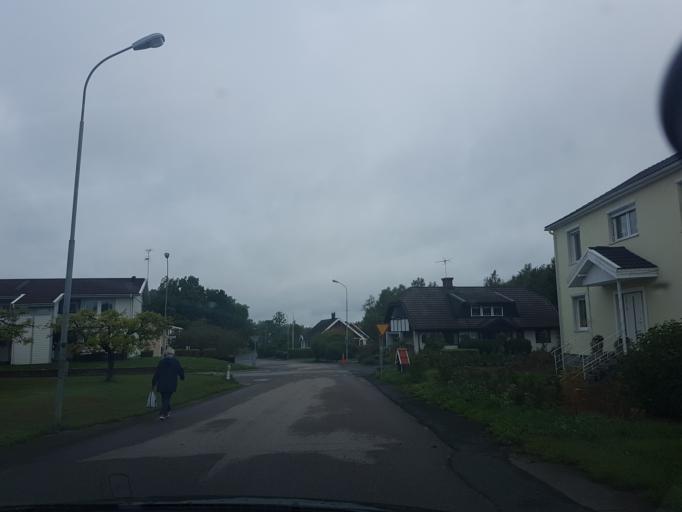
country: SE
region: Joenkoeping
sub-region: Vetlanda Kommun
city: Vetlanda
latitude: 57.3030
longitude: 15.1280
